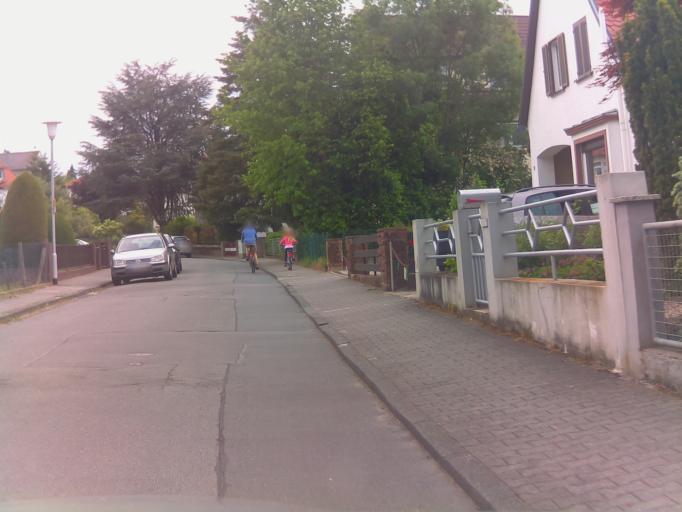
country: DE
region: Hesse
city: Ober-Ramstadt
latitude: 49.8300
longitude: 8.7347
